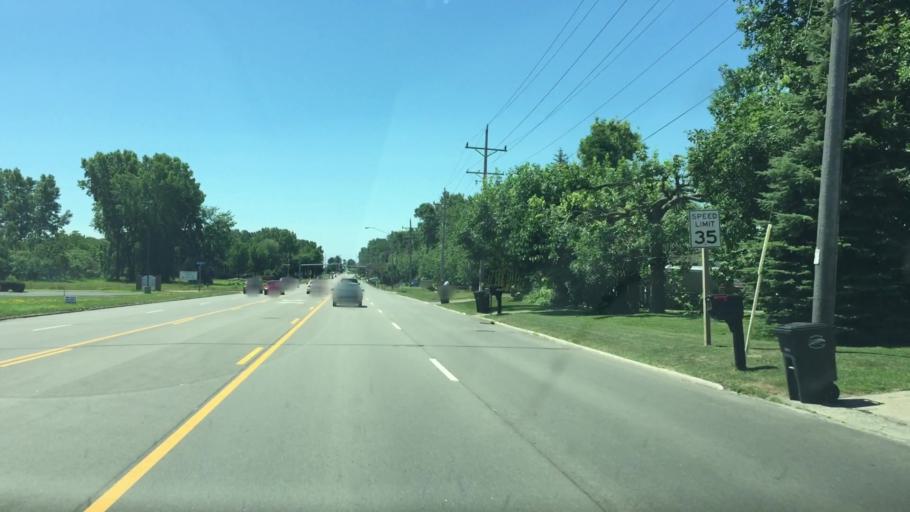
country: US
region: Wisconsin
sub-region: Outagamie County
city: Appleton
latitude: 44.2219
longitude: -88.4042
